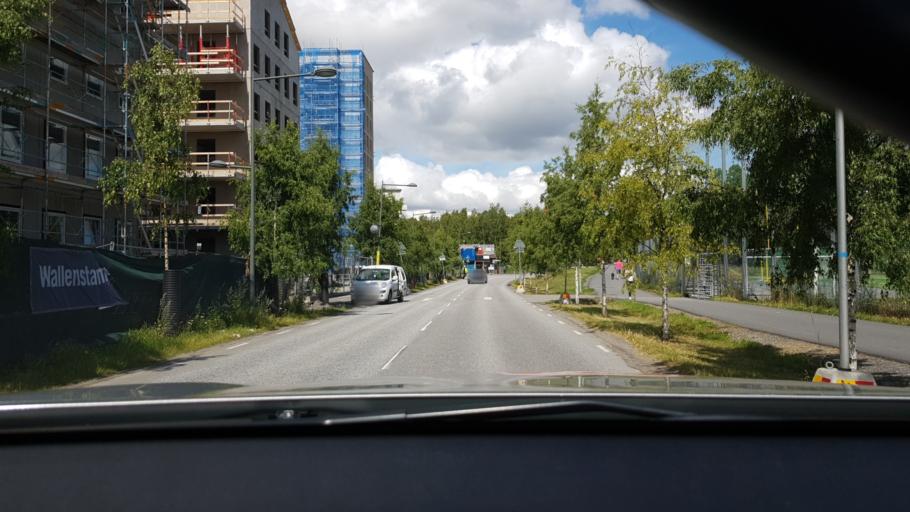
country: SE
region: Stockholm
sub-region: Tyreso Kommun
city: Bollmora
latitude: 59.2468
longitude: 18.2236
